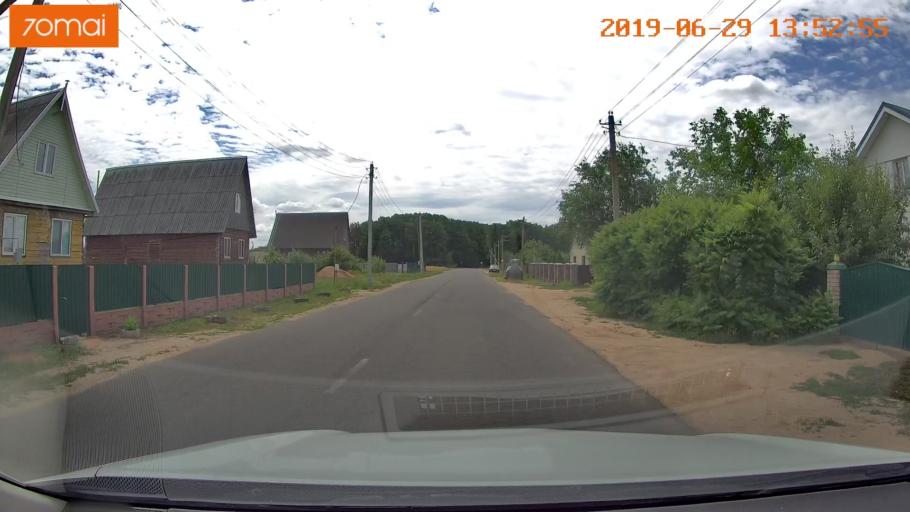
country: BY
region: Minsk
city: Slutsk
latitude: 52.9923
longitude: 27.5501
